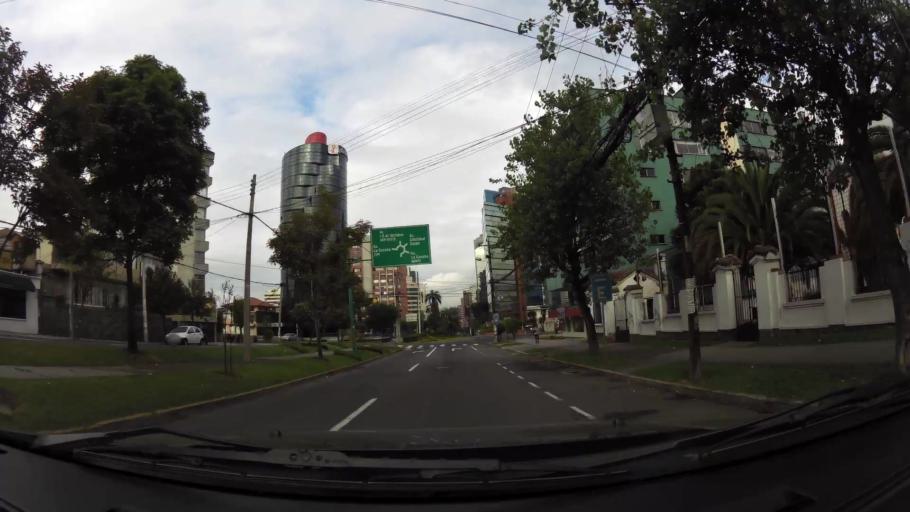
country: EC
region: Pichincha
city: Quito
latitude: -0.2031
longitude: -78.4823
